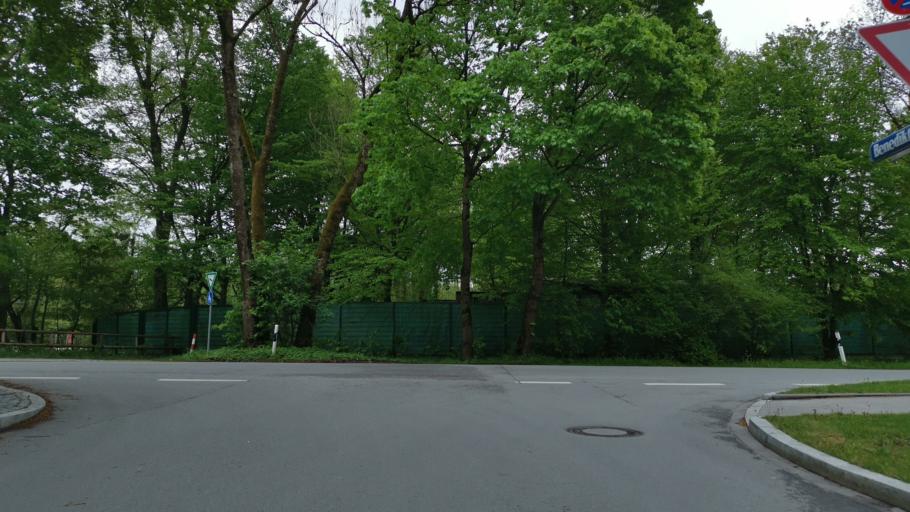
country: DE
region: Bavaria
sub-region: Upper Bavaria
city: Pullach im Isartal
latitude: 48.0947
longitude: 11.5453
